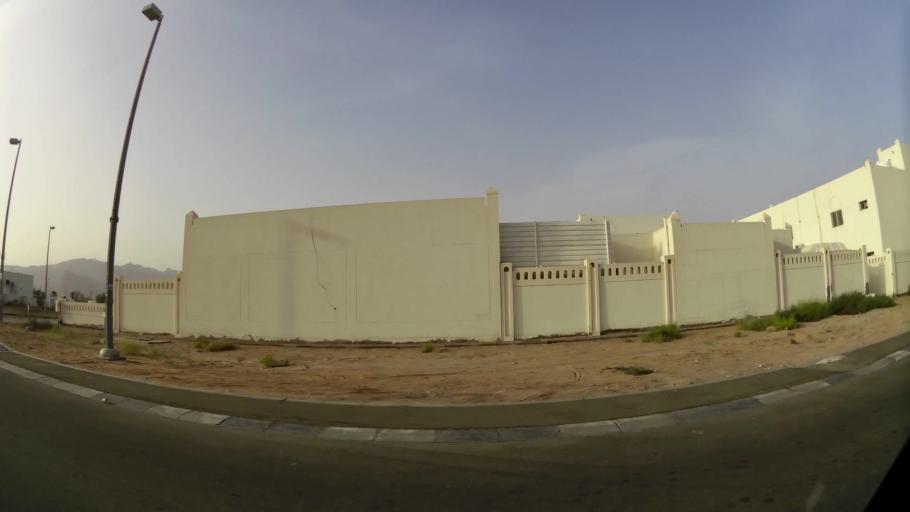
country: AE
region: Abu Dhabi
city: Al Ain
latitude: 24.1140
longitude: 55.7137
